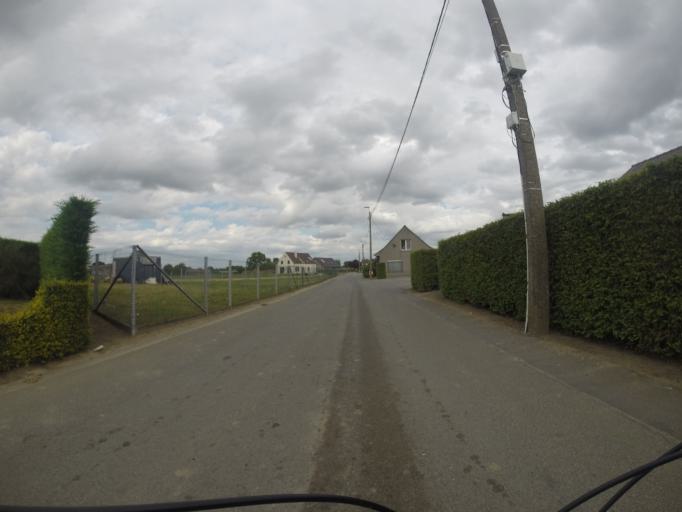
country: BE
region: Flanders
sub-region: Provincie West-Vlaanderen
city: Hooglede
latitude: 50.9489
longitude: 3.0789
